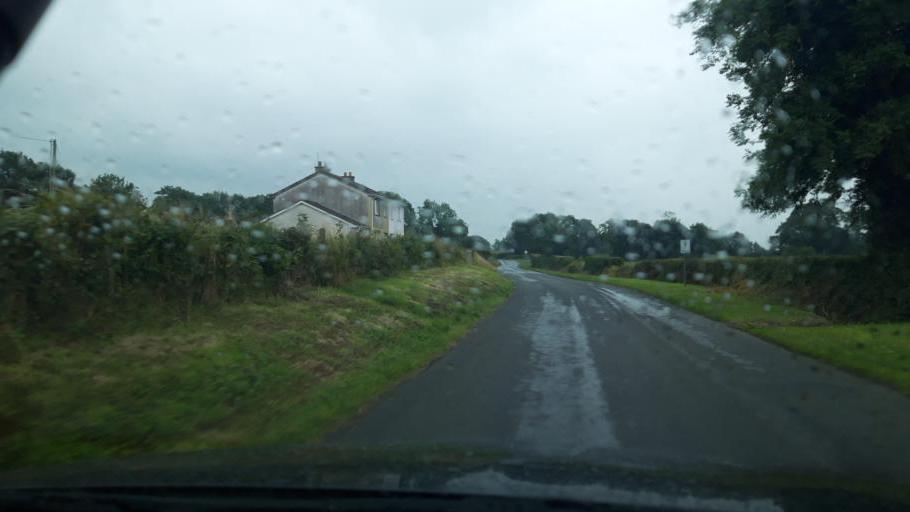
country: IE
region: Leinster
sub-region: Kilkenny
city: Callan
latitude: 52.6608
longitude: -7.4371
